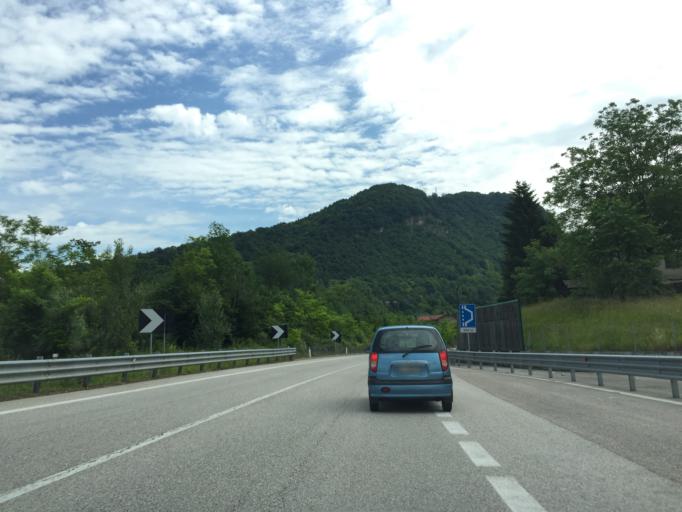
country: IT
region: Veneto
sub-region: Provincia di Belluno
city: Feltre
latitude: 46.0118
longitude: 11.9159
